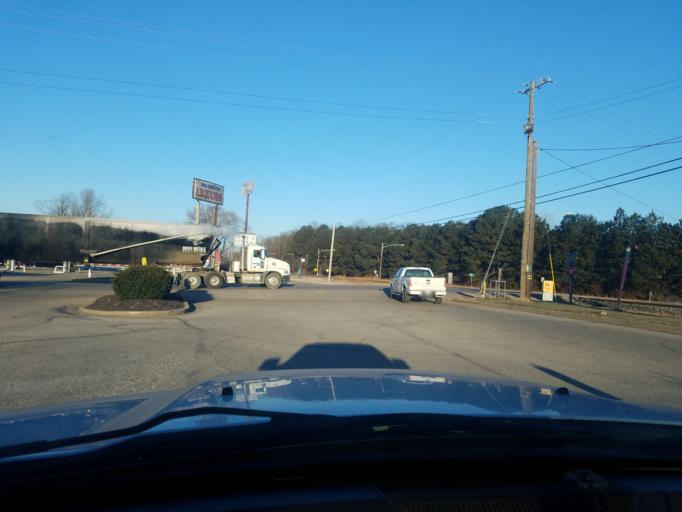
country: US
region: Kentucky
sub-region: Bullitt County
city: Lebanon Junction
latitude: 37.8282
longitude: -85.7244
